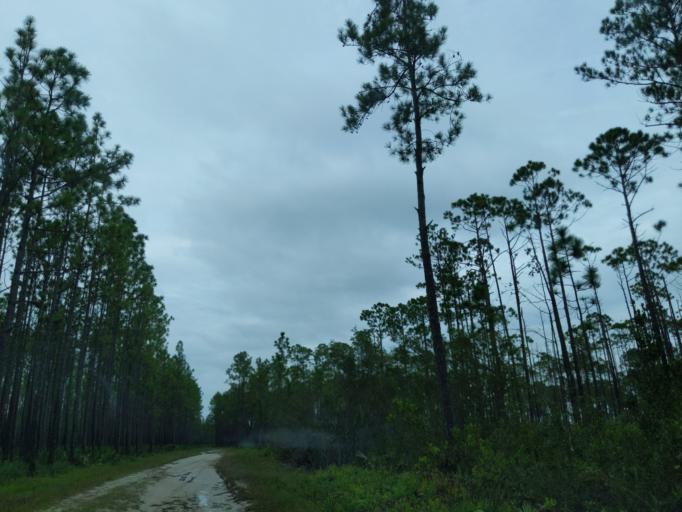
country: US
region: Florida
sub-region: Gadsden County
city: Midway
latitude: 30.3497
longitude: -84.4912
